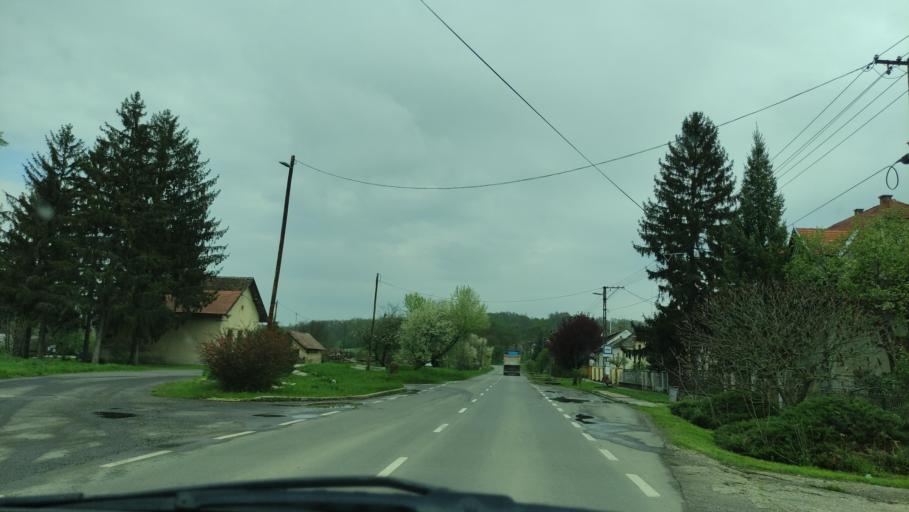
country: HU
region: Baranya
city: Komlo
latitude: 46.2158
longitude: 18.2426
